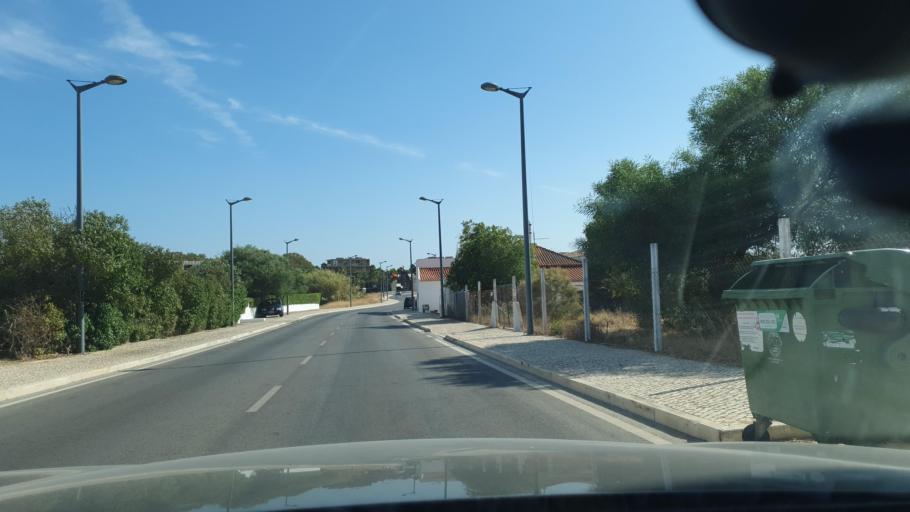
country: PT
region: Faro
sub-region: Albufeira
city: Guia
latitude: 37.0975
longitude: -8.3180
